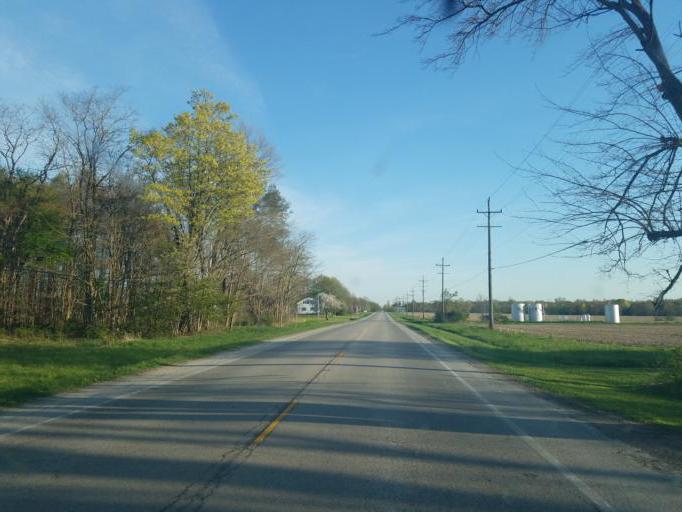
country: US
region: Ohio
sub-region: Ashtabula County
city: Conneaut
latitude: 41.8054
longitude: -80.5722
